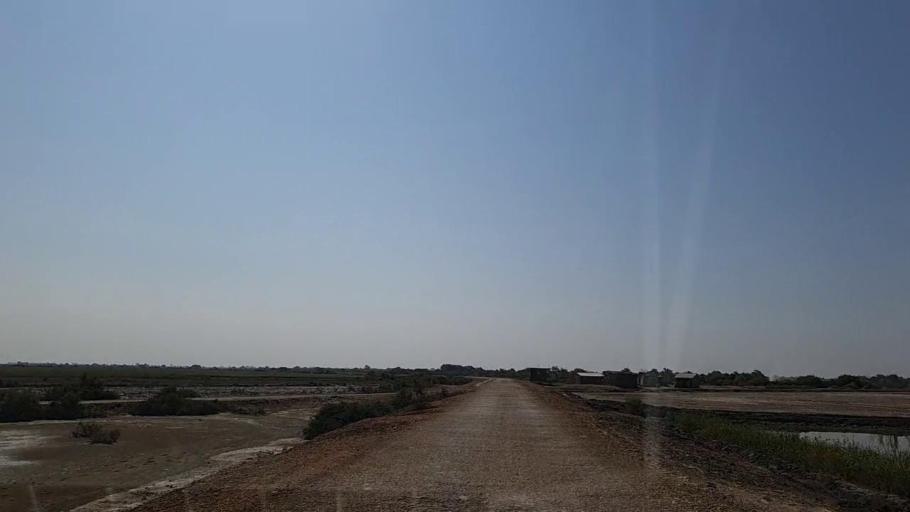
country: PK
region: Sindh
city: Chuhar Jamali
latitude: 24.4755
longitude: 68.0912
